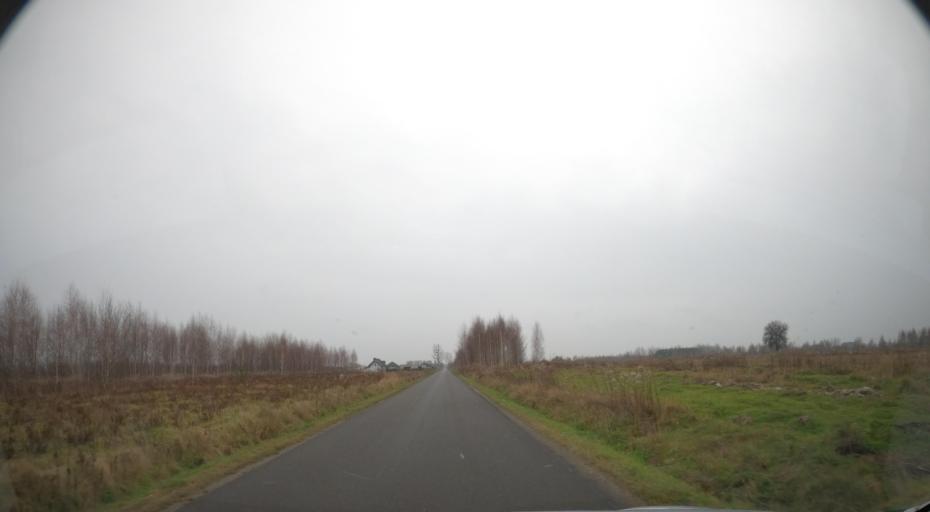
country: PL
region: Masovian Voivodeship
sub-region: Powiat radomski
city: Jastrzebia
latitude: 51.4211
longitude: 21.2425
